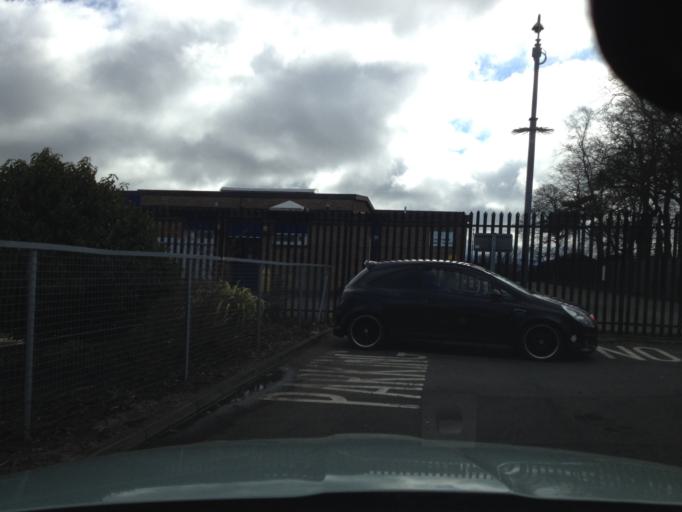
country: GB
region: Scotland
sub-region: West Lothian
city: Livingston
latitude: 55.9004
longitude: -3.5197
